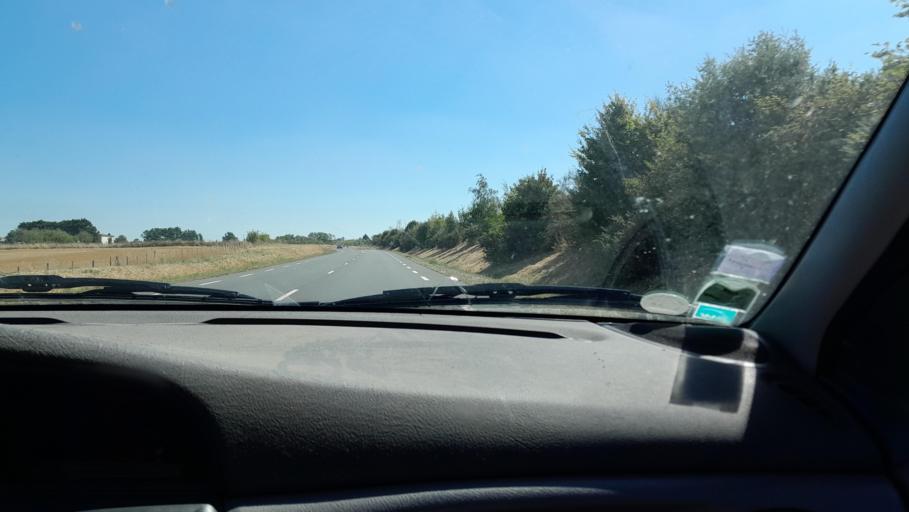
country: FR
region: Pays de la Loire
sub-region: Departement de la Loire-Atlantique
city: Saint-Gereon
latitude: 47.3754
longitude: -1.2118
